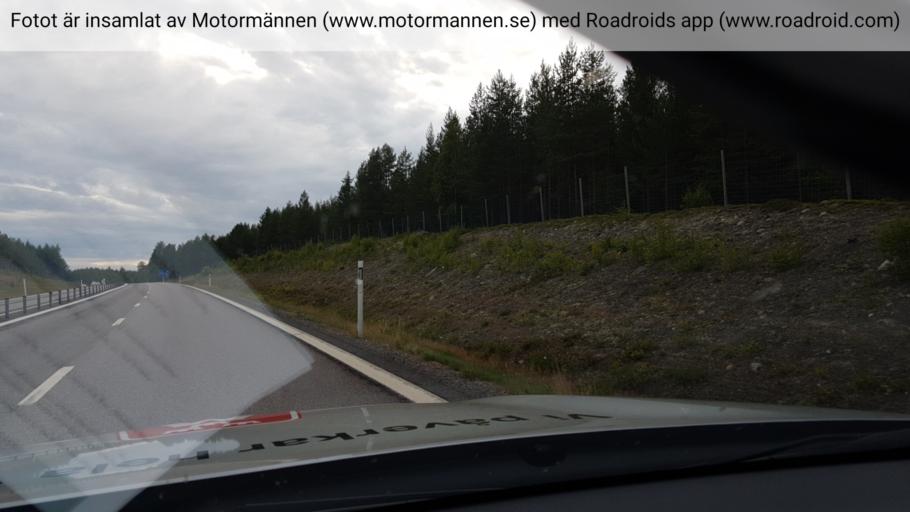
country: SE
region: Norrbotten
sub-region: Lulea Kommun
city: Ranea
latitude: 65.8737
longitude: 22.3749
